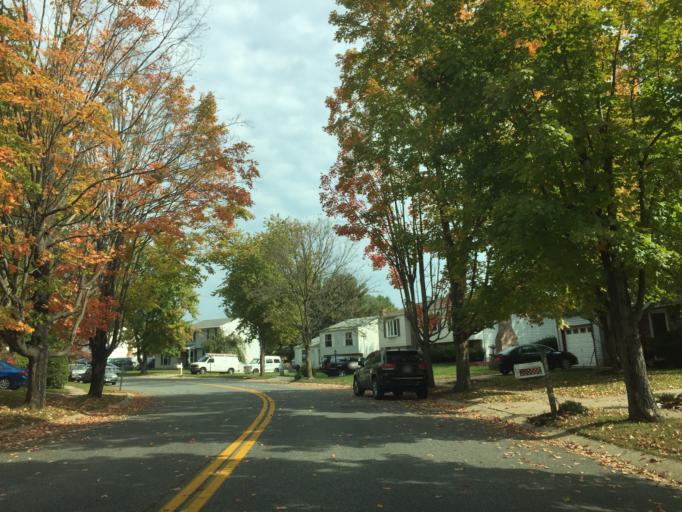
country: US
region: Maryland
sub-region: Harford County
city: Bel Air South
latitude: 39.4816
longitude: -76.2991
